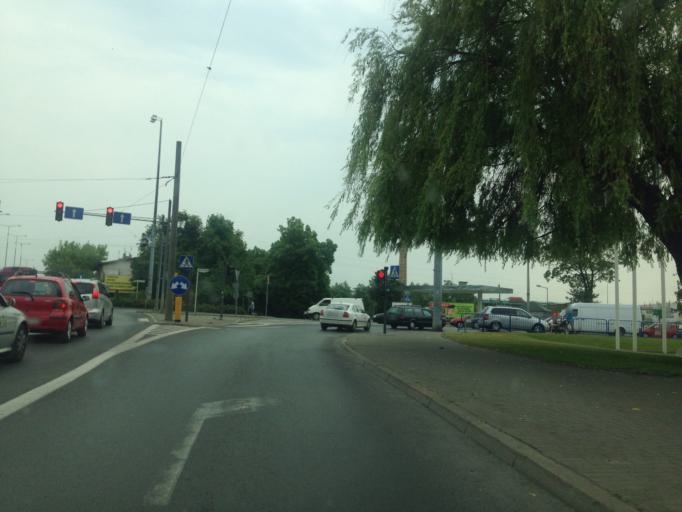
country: PL
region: Kujawsko-Pomorskie
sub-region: Grudziadz
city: Grudziadz
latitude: 53.4843
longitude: 18.7533
